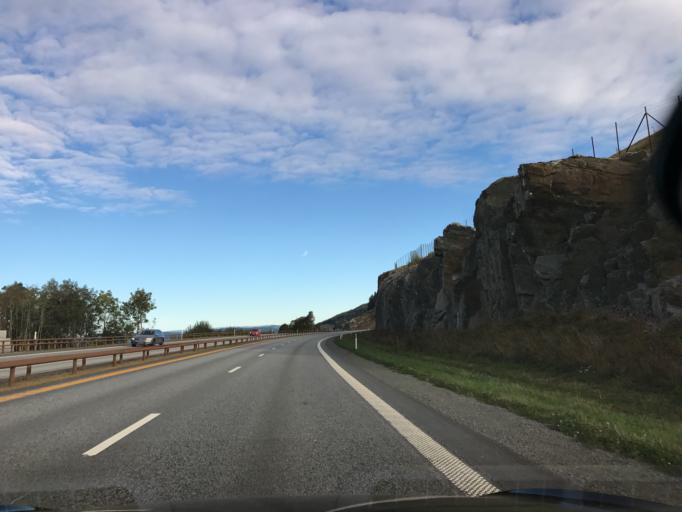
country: NO
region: Akershus
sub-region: Eidsvoll
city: Eidsvoll
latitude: 60.4954
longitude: 11.2369
